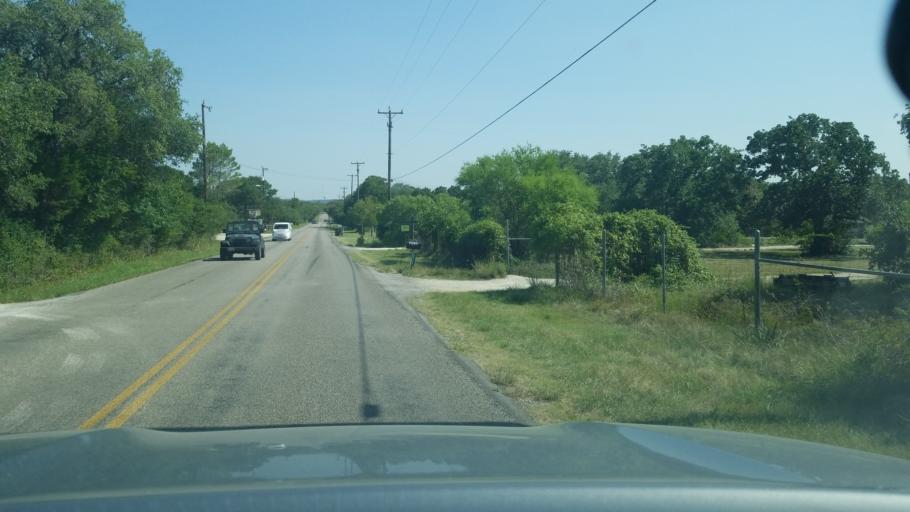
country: US
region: Texas
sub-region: Bexar County
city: Timberwood Park
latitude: 29.7520
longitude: -98.5128
